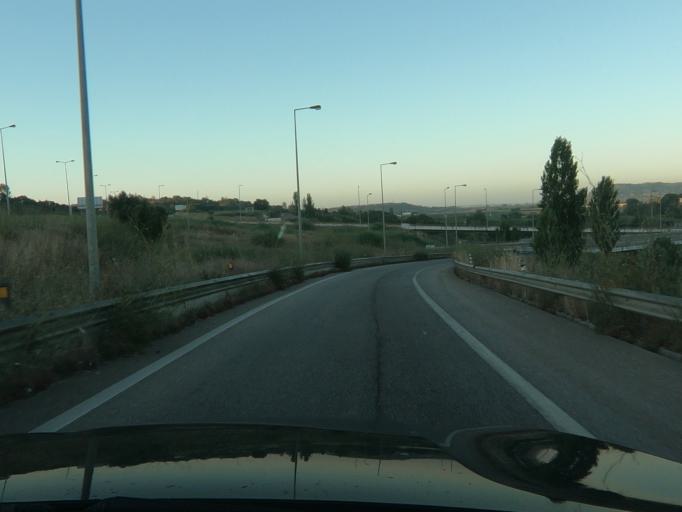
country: PT
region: Santarem
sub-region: Santarem
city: Santarem
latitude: 39.2316
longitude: -8.7058
